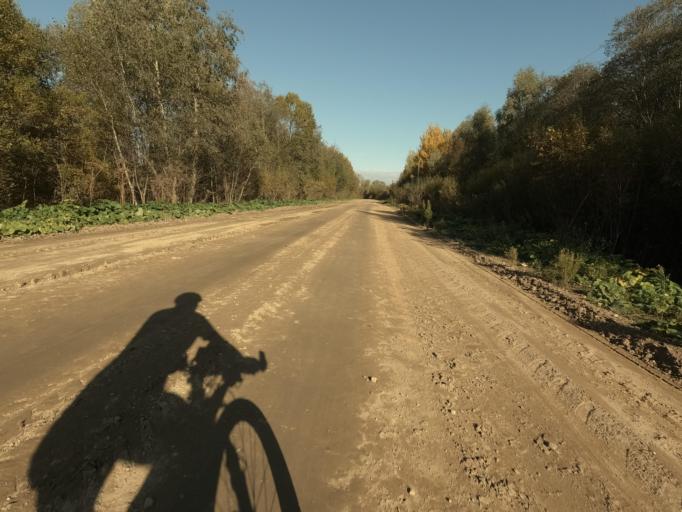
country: RU
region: Novgorod
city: Batetskiy
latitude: 58.8778
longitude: 30.7265
